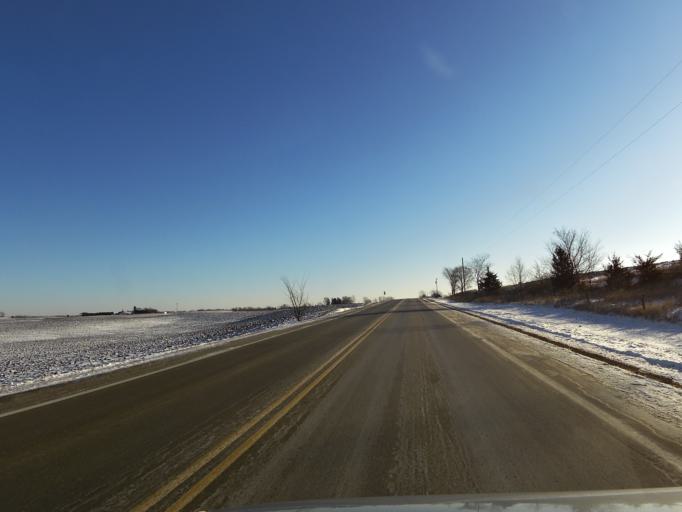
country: US
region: Minnesota
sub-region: Carver County
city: Chaska
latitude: 44.7326
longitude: -93.5607
